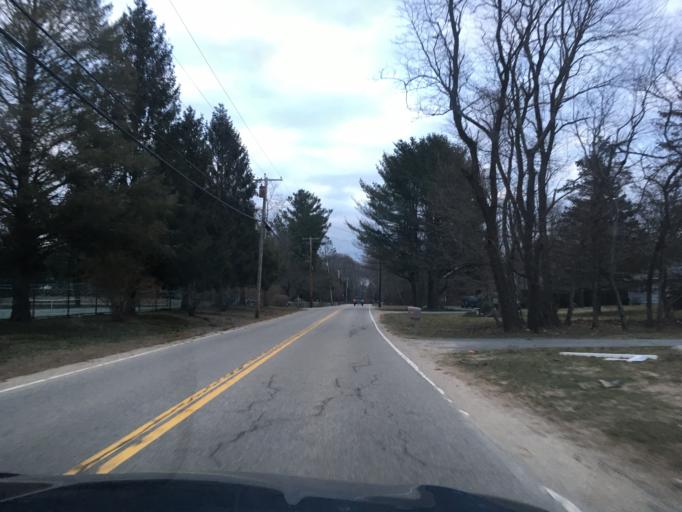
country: US
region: Rhode Island
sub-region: Washington County
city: Exeter
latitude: 41.6236
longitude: -71.5205
